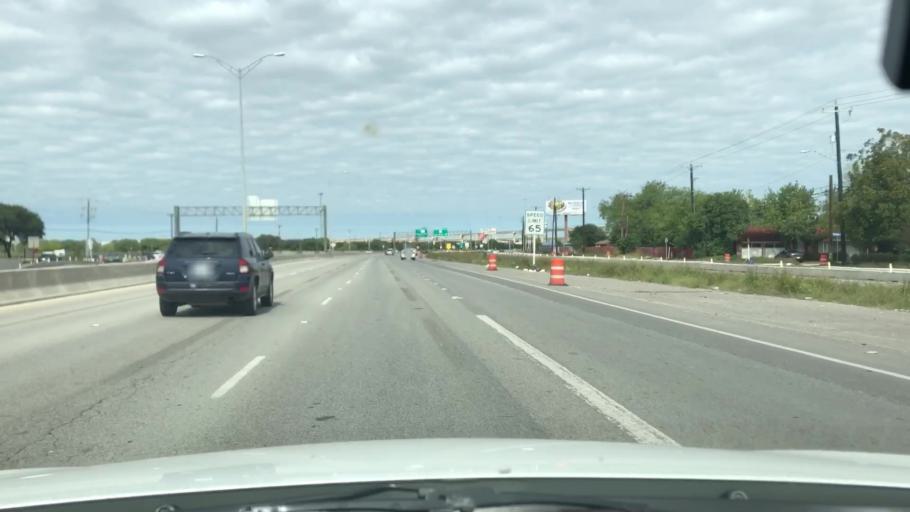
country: US
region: Texas
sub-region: Bexar County
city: Lackland Air Force Base
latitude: 29.4252
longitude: -98.6496
